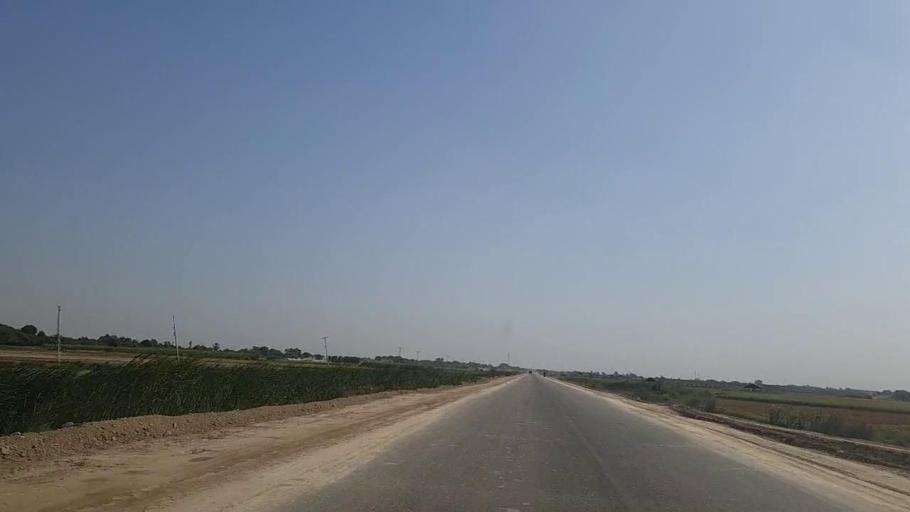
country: PK
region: Sindh
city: Mirpur Batoro
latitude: 24.7495
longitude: 68.2372
